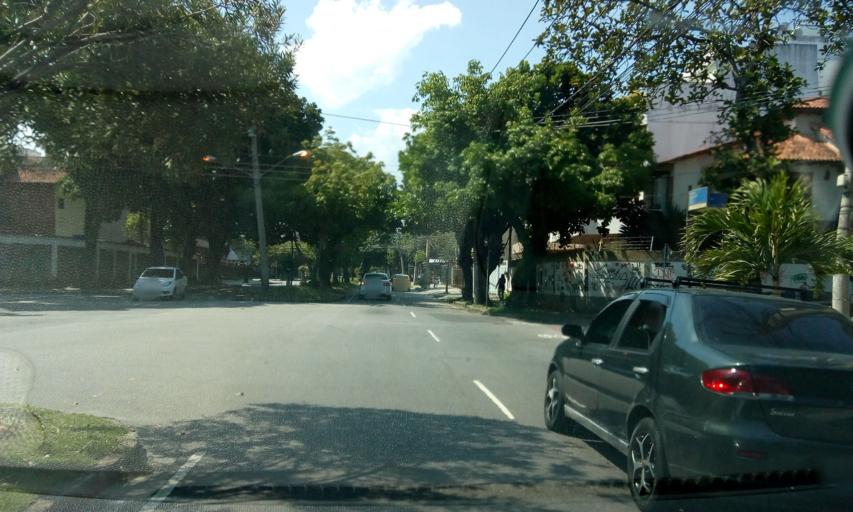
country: BR
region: Rio de Janeiro
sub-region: Nilopolis
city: Nilopolis
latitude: -23.0217
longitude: -43.4584
